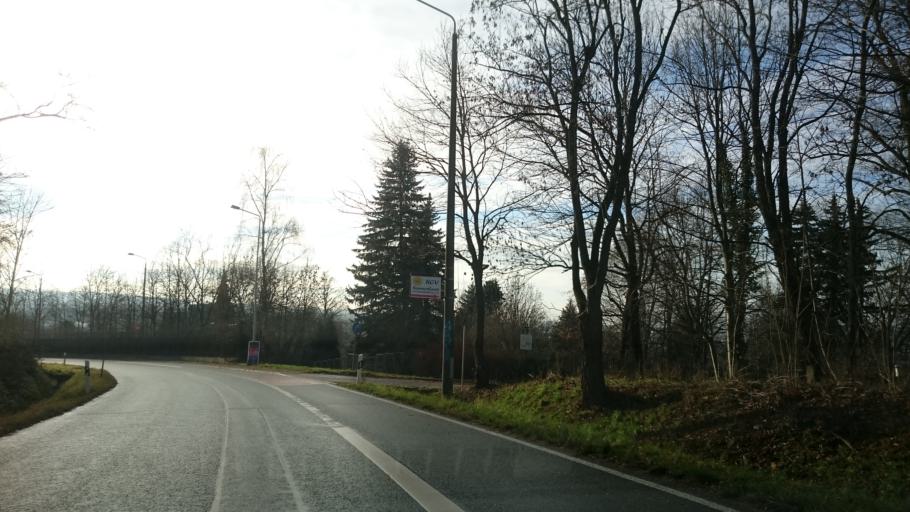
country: DE
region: Saxony
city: Zwickau
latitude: 50.7183
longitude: 12.5049
